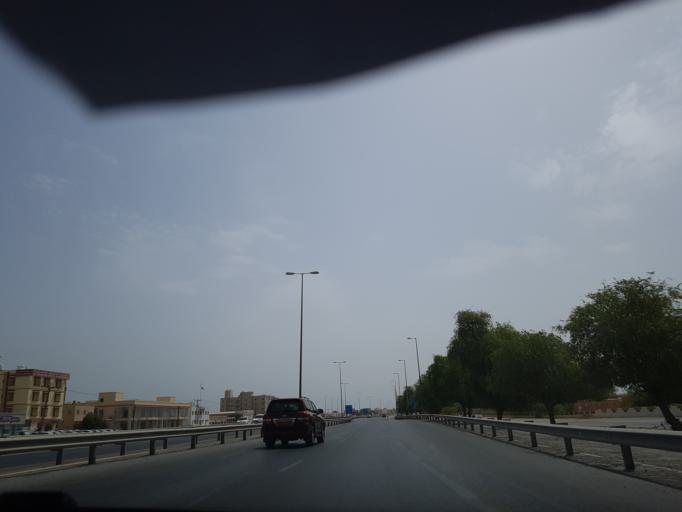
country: OM
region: Al Batinah
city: As Suwayq
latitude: 23.7563
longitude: 57.5888
